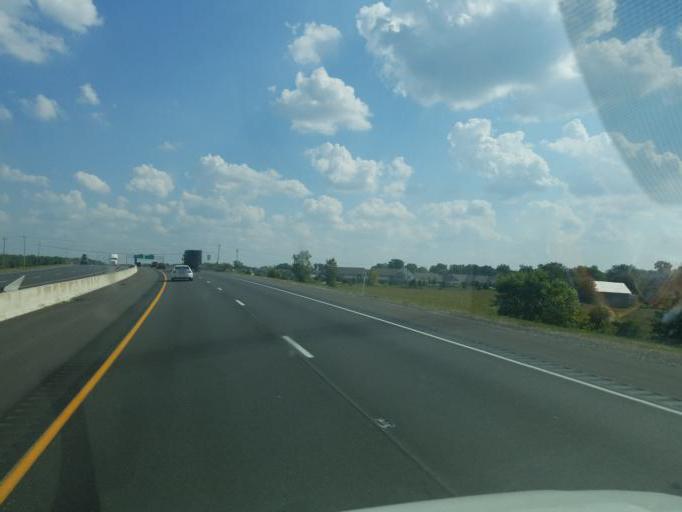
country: US
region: Indiana
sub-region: Allen County
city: Fort Wayne
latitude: 41.1626
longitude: -85.0727
